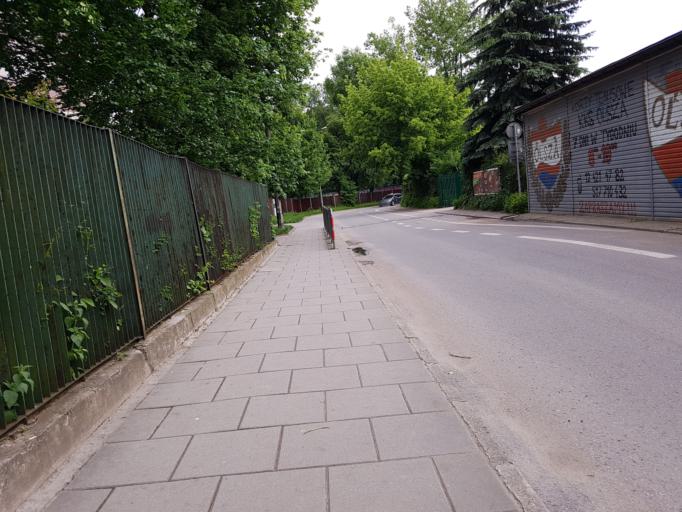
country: PL
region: Lesser Poland Voivodeship
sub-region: Krakow
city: Krakow
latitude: 50.0557
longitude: 19.9501
